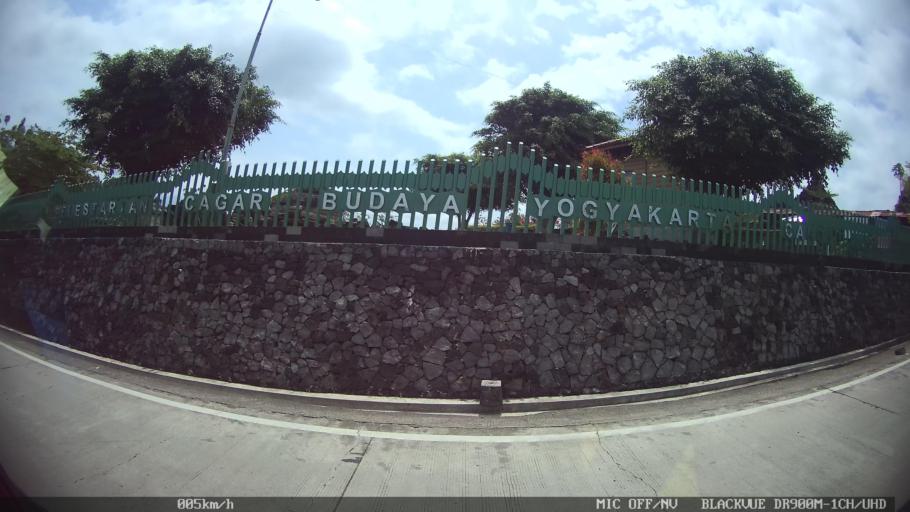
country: ID
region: Central Java
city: Candi Prambanan
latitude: -7.7841
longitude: 110.5114
